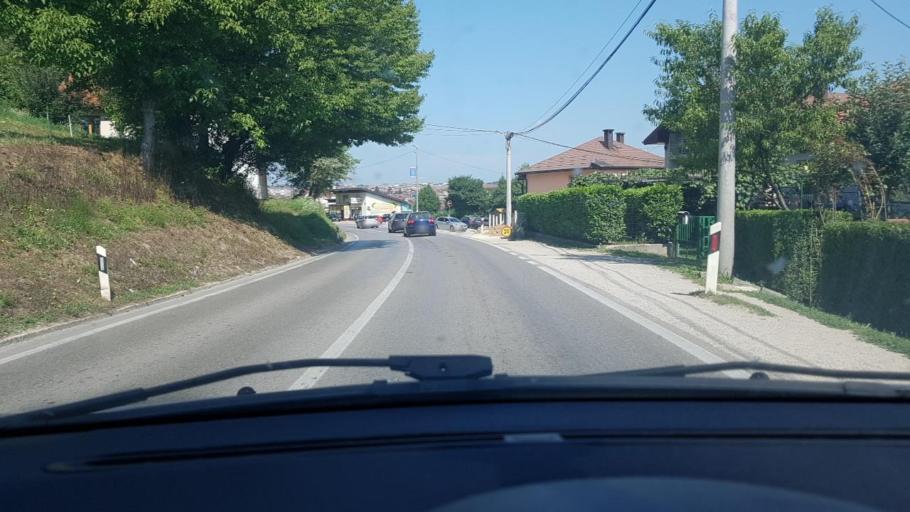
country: BA
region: Federation of Bosnia and Herzegovina
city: Velika Kladusa
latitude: 45.1790
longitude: 15.8204
